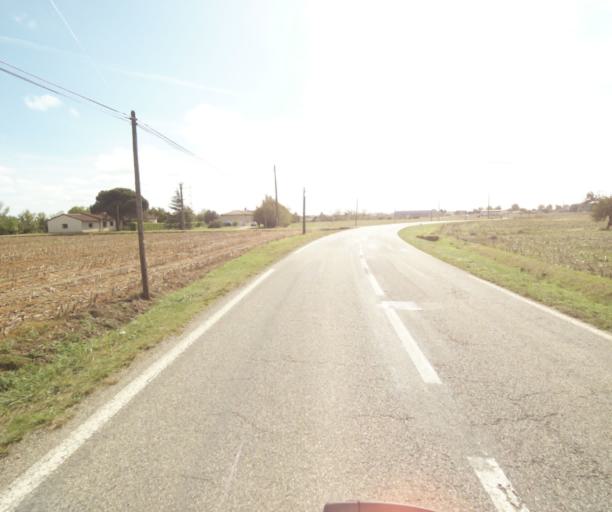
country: FR
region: Midi-Pyrenees
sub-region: Departement du Tarn-et-Garonne
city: Saint-Porquier
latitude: 43.9520
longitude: 1.1607
